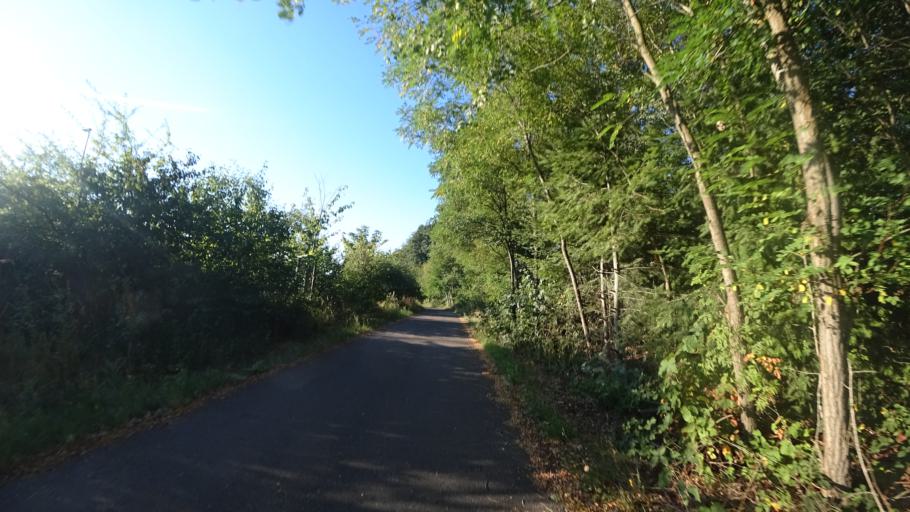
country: DE
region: Rheinland-Pfalz
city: Kratzenburg
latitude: 50.2063
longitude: 7.5512
